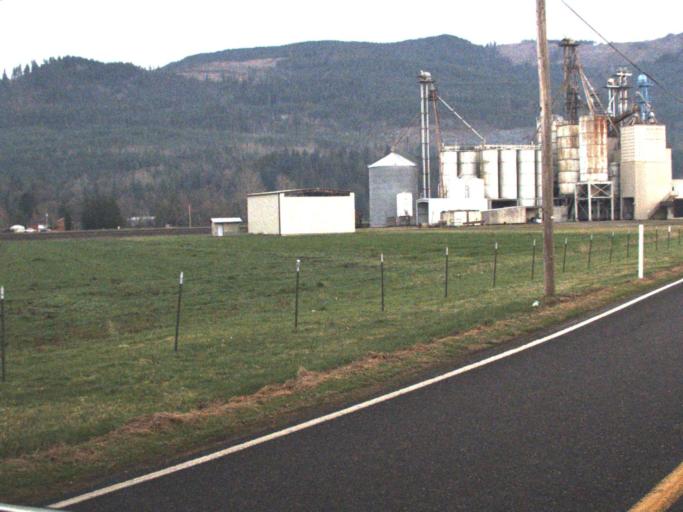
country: US
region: Washington
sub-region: Whatcom County
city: Nooksack
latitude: 48.8582
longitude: -122.2980
